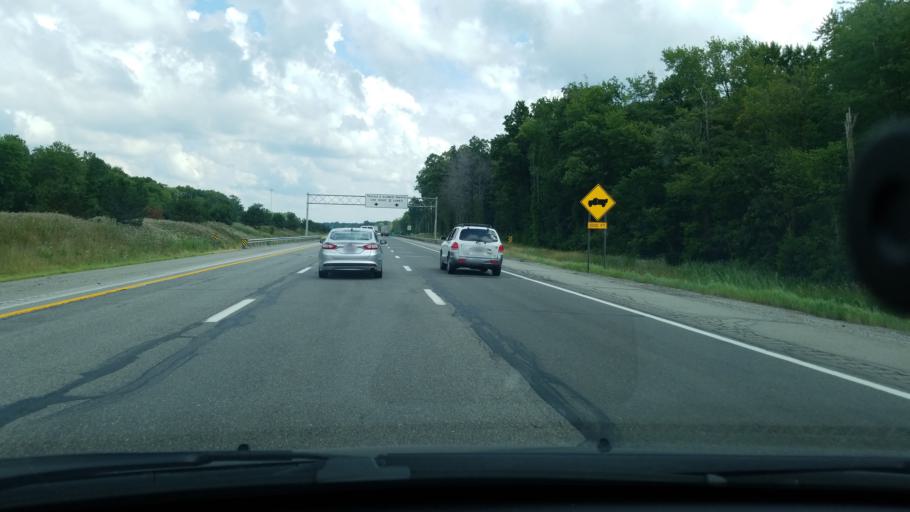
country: US
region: Ohio
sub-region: Summit County
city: Richfield
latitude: 41.2662
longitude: -81.6160
